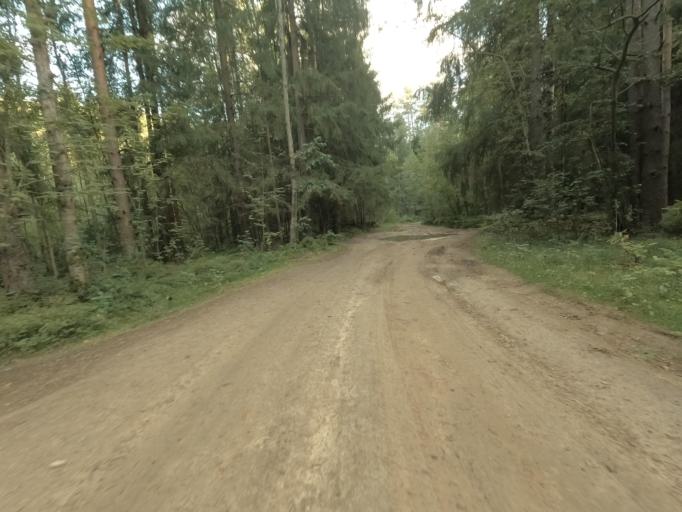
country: RU
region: Leningrad
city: Otradnoye
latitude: 59.8517
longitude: 30.7963
